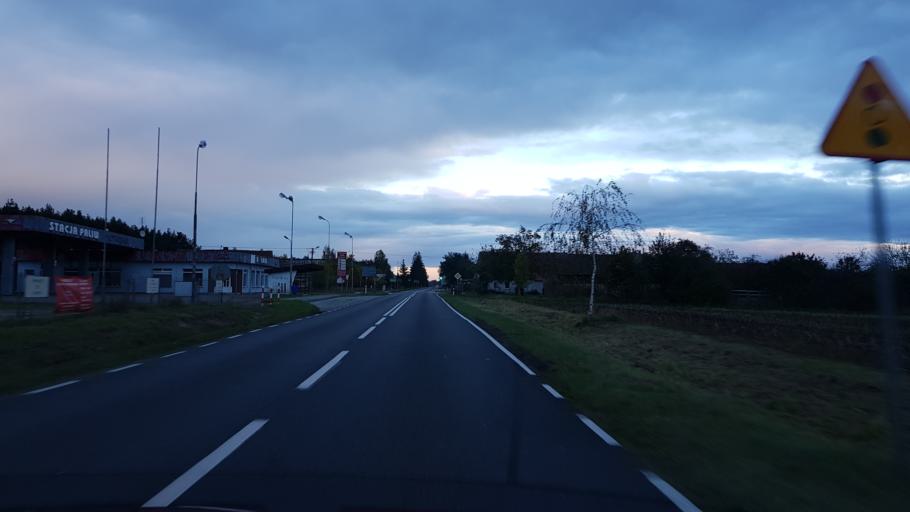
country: PL
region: Greater Poland Voivodeship
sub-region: Powiat zlotowski
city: Krajenka
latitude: 53.2620
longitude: 16.9189
